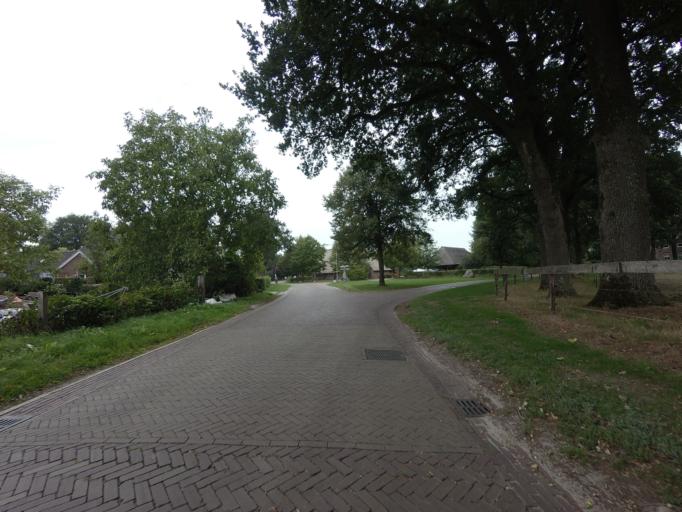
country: NL
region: Drenthe
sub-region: Gemeente Assen
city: Assen
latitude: 52.9956
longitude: 6.6321
